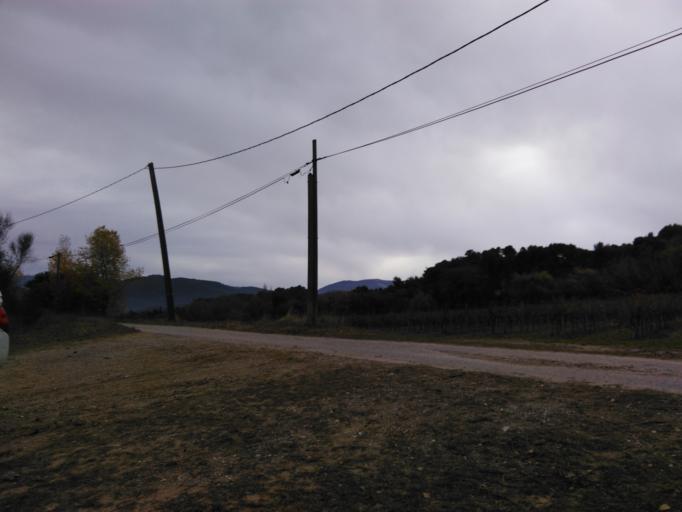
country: FR
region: Rhone-Alpes
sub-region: Departement de la Drome
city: Mirabel-aux-Baronnies
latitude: 44.2756
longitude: 5.0980
